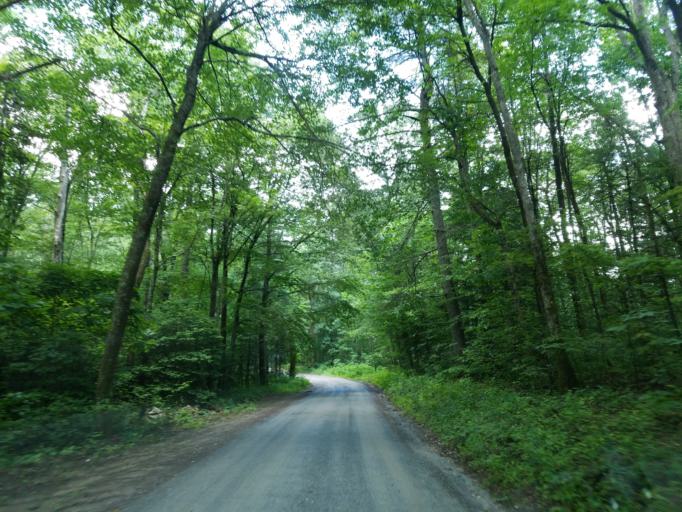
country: US
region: Georgia
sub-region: Fannin County
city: Blue Ridge
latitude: 34.6493
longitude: -84.2157
